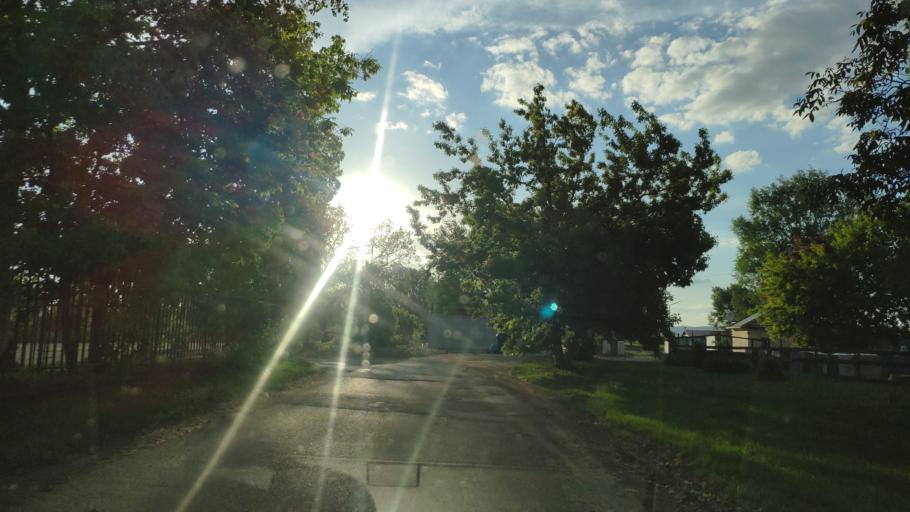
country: SK
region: Kosicky
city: Kosice
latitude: 48.6587
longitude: 21.3139
